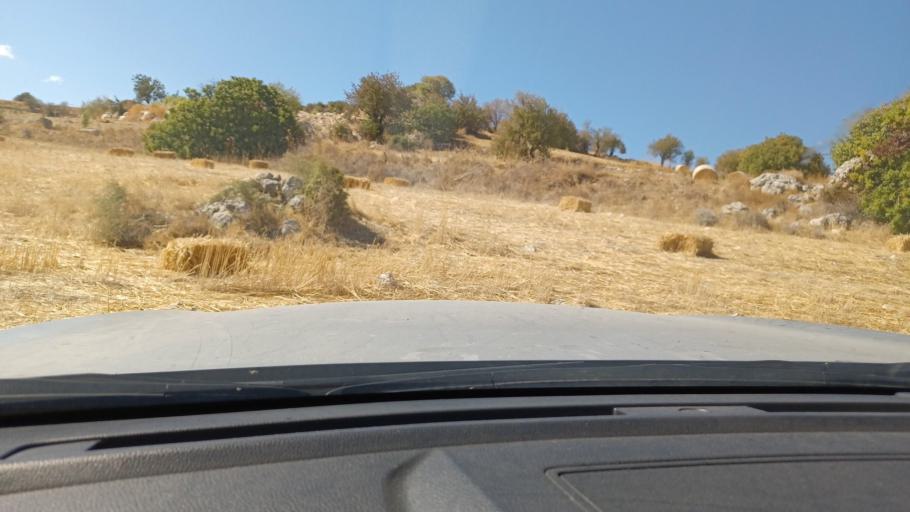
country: CY
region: Pafos
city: Polis
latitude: 34.9682
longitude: 32.5110
